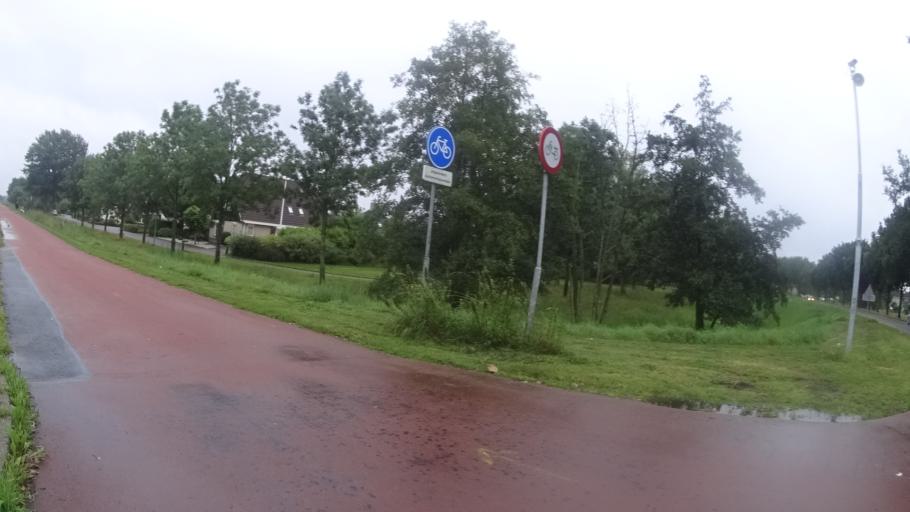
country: NL
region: Groningen
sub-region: Gemeente  Oldambt
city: Winschoten
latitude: 53.1614
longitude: 7.0236
